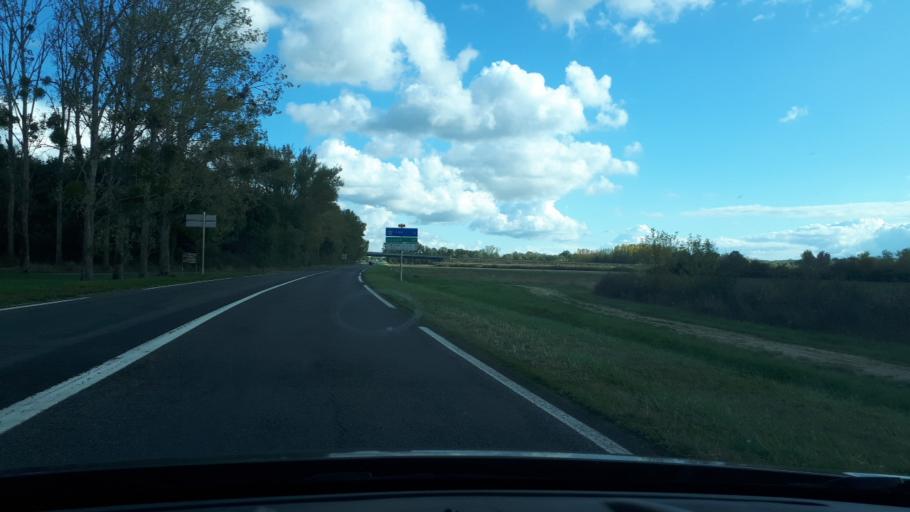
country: FR
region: Centre
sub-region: Departement du Loir-et-Cher
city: Mareuil-sur-Cher
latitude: 47.3079
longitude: 1.3409
